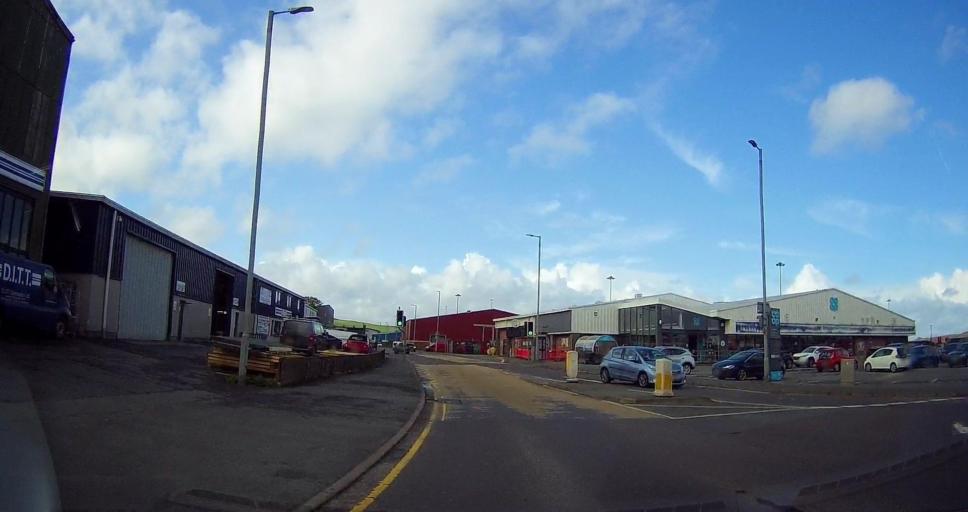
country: GB
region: Scotland
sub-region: Shetland Islands
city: Lerwick
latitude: 60.1588
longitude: -1.1568
